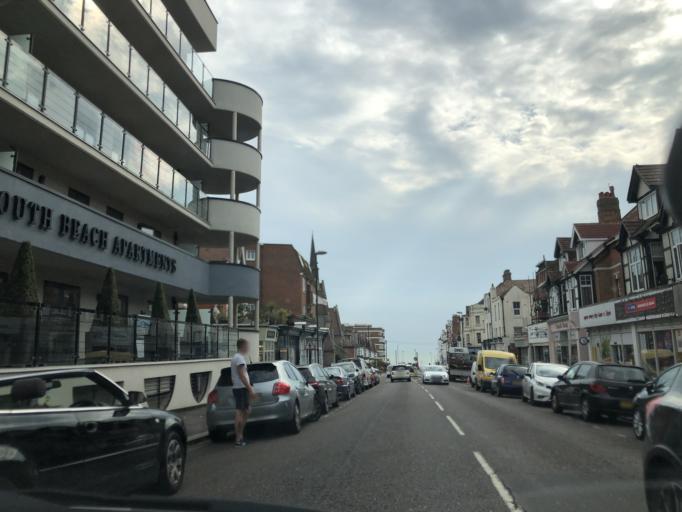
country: GB
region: England
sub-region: East Sussex
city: Bexhill-on-Sea
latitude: 50.8405
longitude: 0.4773
